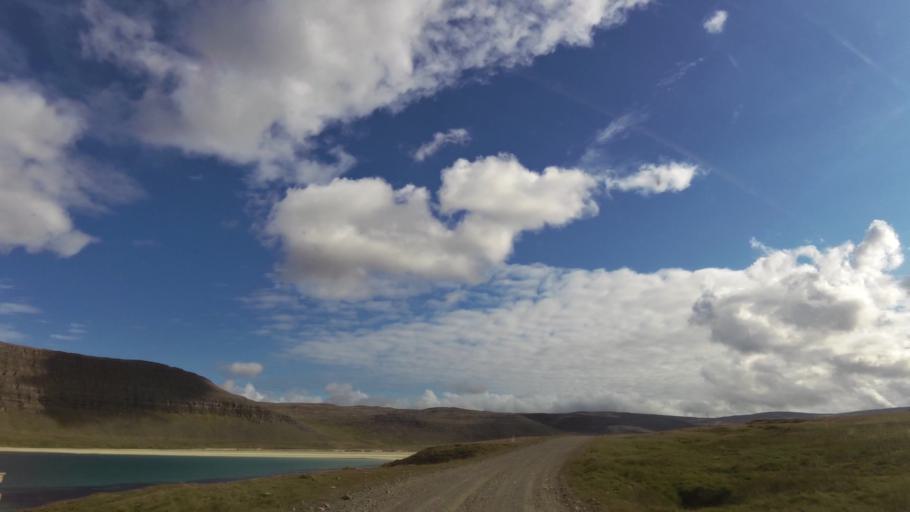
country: IS
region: West
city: Olafsvik
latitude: 65.5907
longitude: -24.1237
